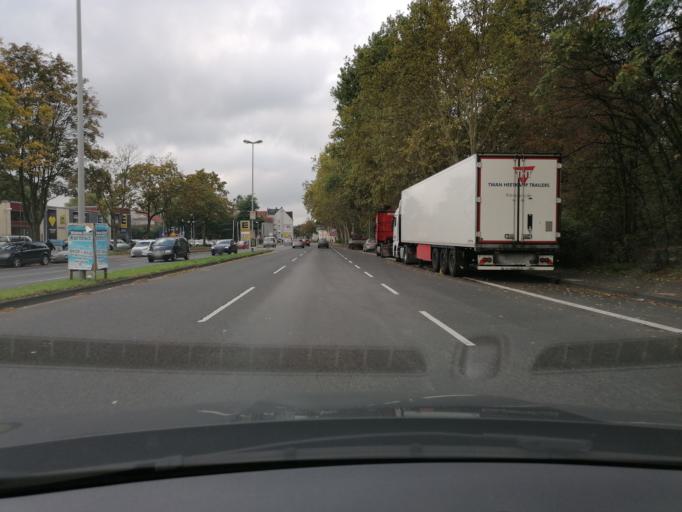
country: DE
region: North Rhine-Westphalia
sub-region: Regierungsbezirk Munster
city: Gelsenkirchen
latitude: 51.5396
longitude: 7.1494
